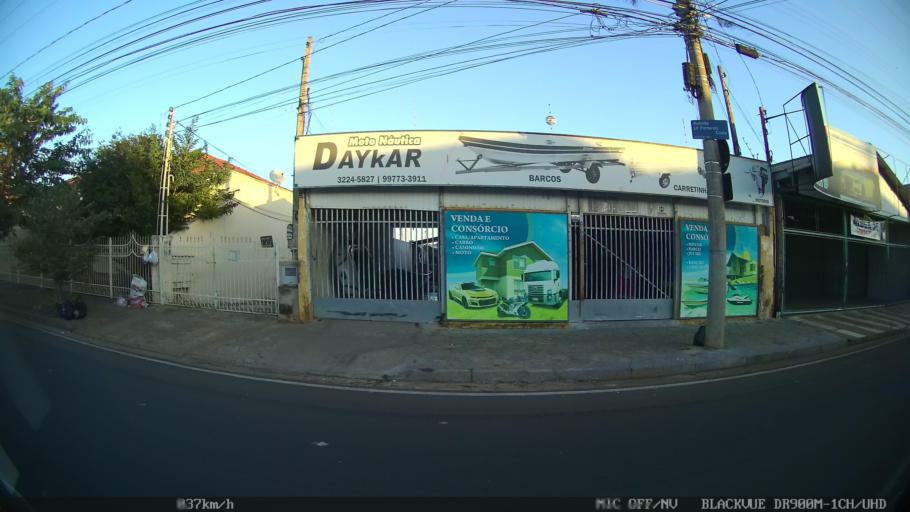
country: BR
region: Sao Paulo
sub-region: Sao Jose Do Rio Preto
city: Sao Jose do Rio Preto
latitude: -20.8048
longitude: -49.3681
